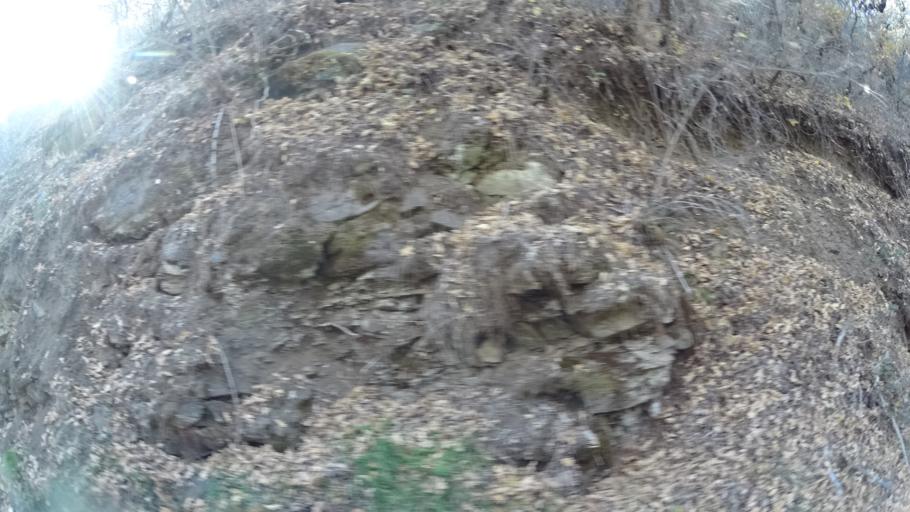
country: US
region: California
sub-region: Siskiyou County
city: Yreka
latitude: 41.8624
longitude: -122.7857
